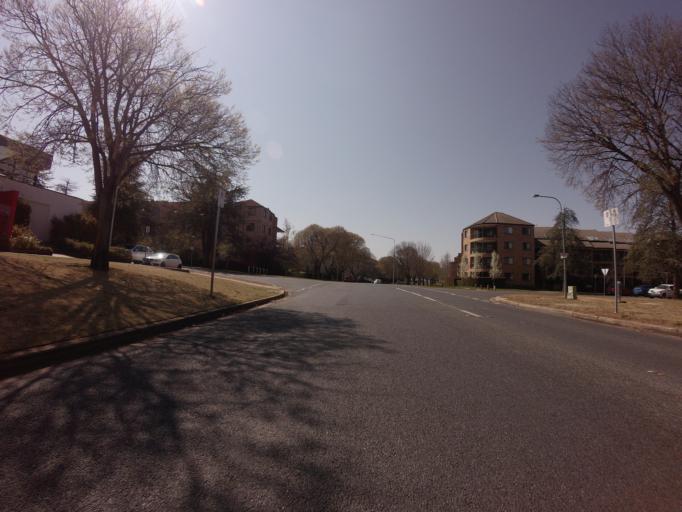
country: AU
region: Australian Capital Territory
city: Forrest
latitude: -35.3196
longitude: 149.1395
